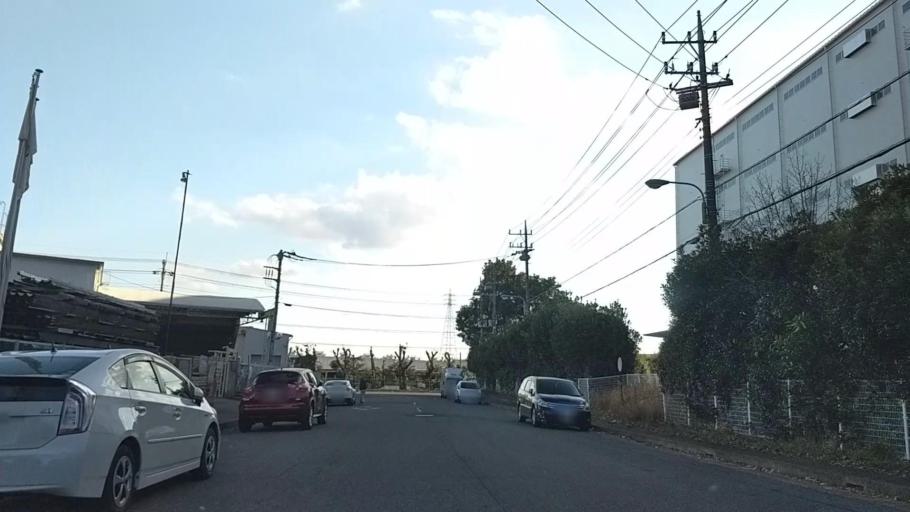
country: JP
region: Kanagawa
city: Atsugi
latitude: 35.4600
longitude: 139.3265
